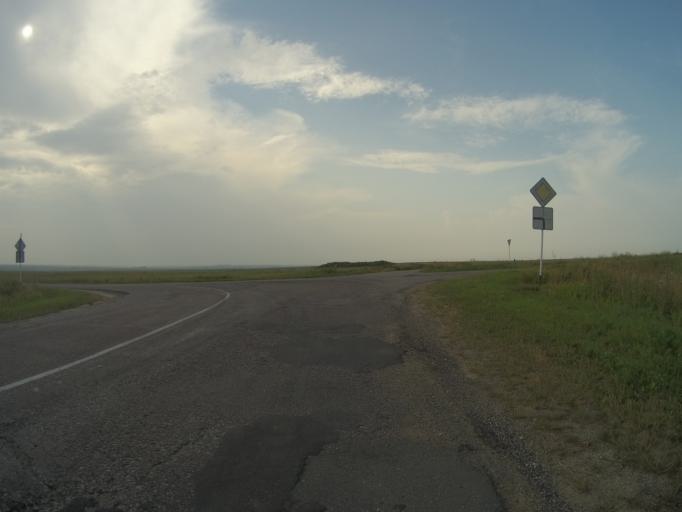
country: RU
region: Vladimir
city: Suzdal'
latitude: 56.3737
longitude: 40.3565
